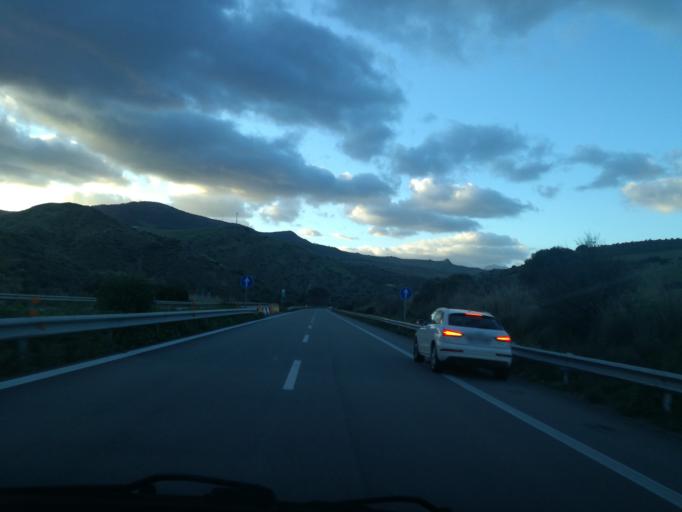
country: IT
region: Sicily
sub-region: Palermo
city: Scillato
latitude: 37.8639
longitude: 13.8771
